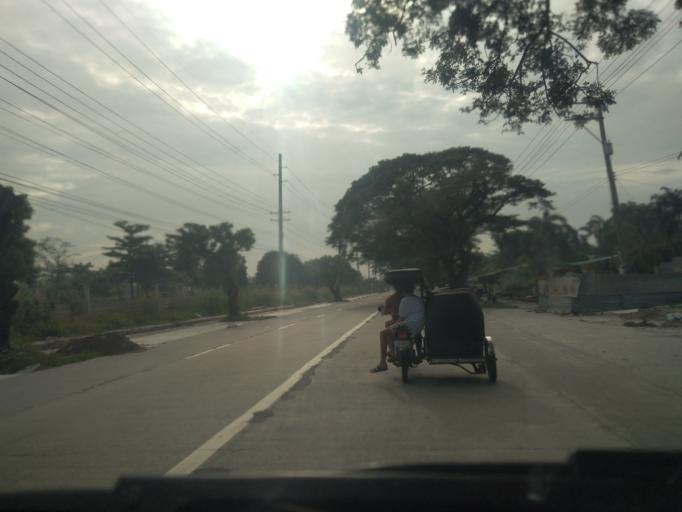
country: PH
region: Central Luzon
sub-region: Province of Pampanga
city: Calibutbut
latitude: 15.1213
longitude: 120.5878
